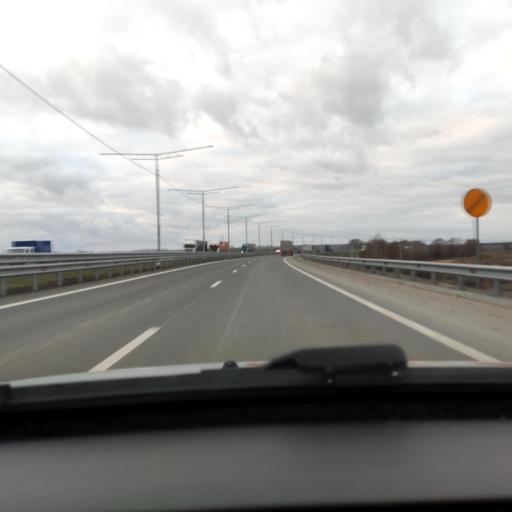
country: RU
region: Lipetsk
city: Khlevnoye
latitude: 52.0588
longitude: 39.1863
